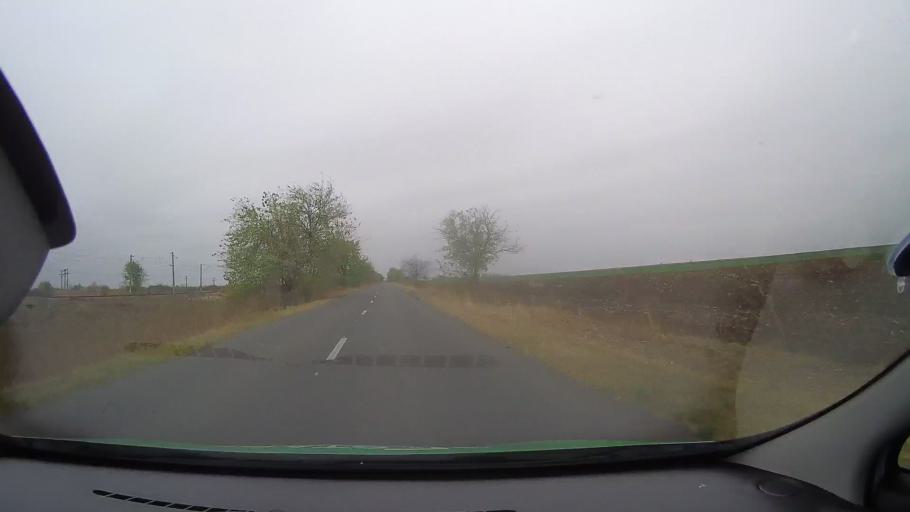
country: RO
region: Ialomita
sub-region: Comuna Valea Ciorii
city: Valea Ciorii
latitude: 44.6930
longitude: 27.6048
